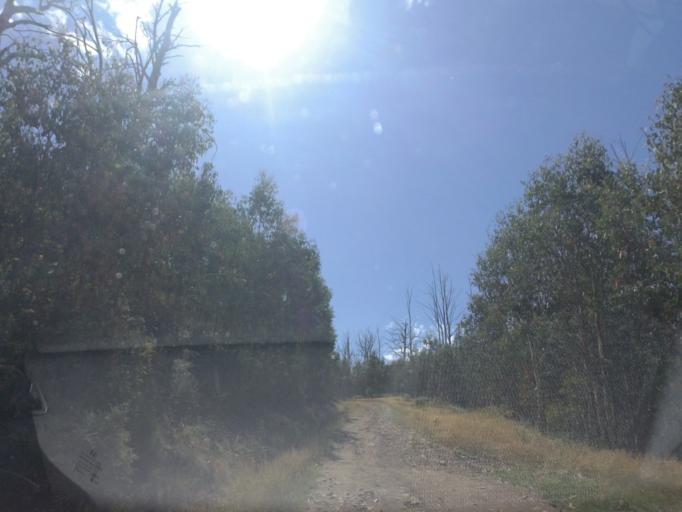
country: AU
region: Victoria
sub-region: Murrindindi
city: Alexandra
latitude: -37.4636
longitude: 145.8508
